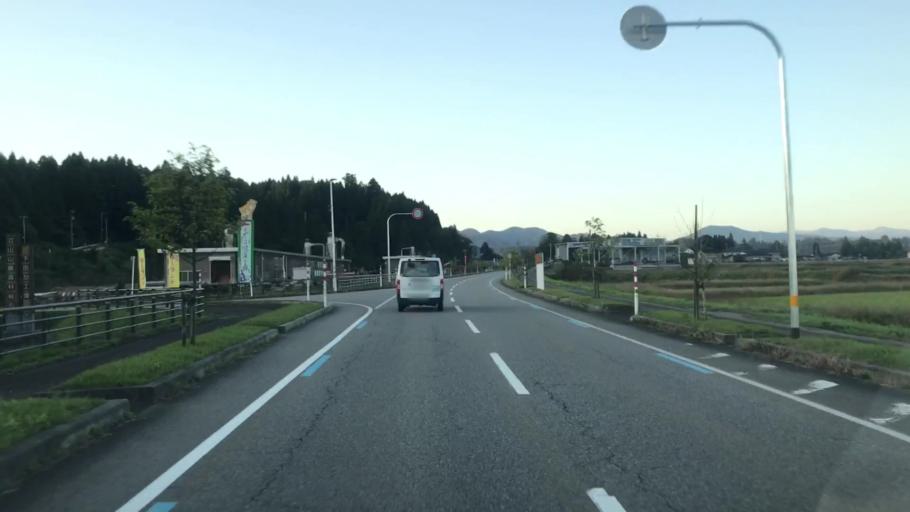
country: JP
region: Toyama
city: Kamiichi
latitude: 36.6196
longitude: 137.3282
